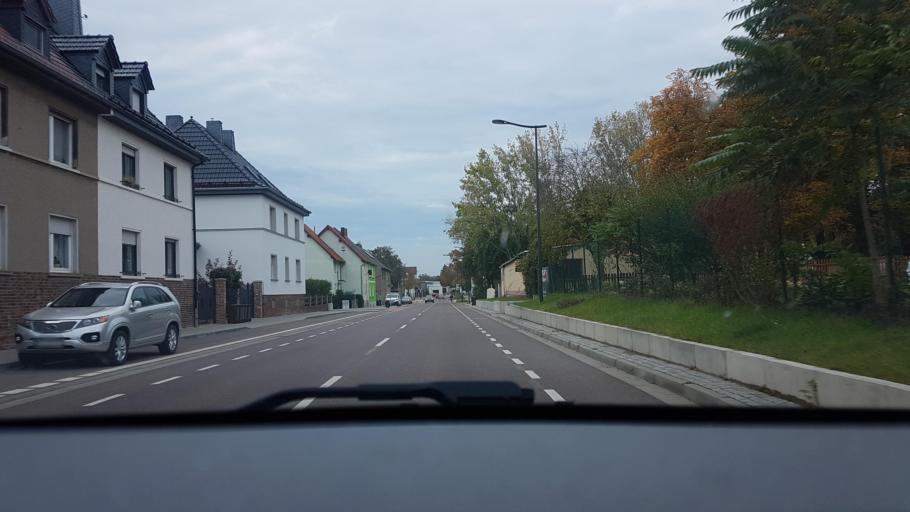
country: DE
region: Saxony-Anhalt
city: Bernburg
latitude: 51.7835
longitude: 11.7625
